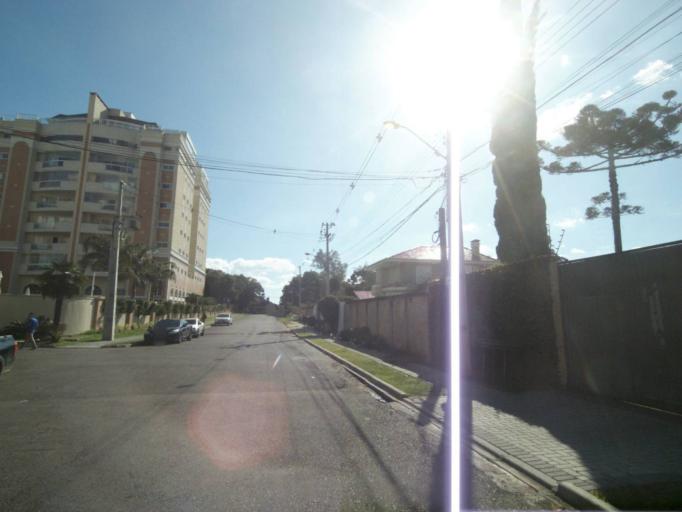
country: BR
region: Parana
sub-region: Curitiba
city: Curitiba
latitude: -25.4440
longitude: -49.3204
